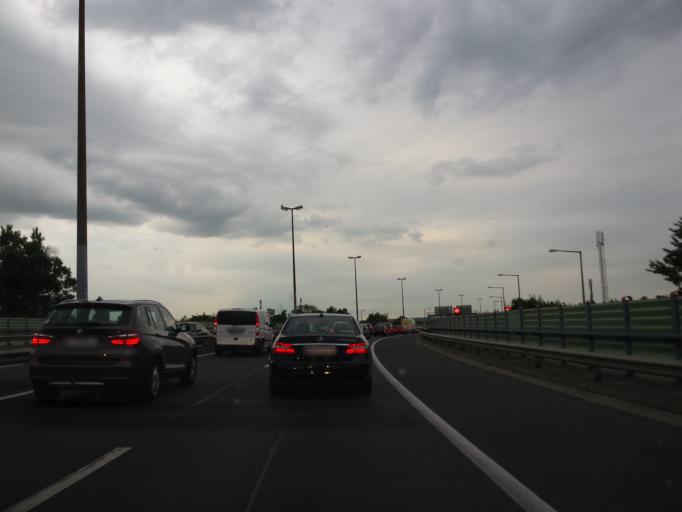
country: AT
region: Vienna
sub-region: Wien Stadt
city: Vienna
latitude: 48.2145
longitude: 16.4468
